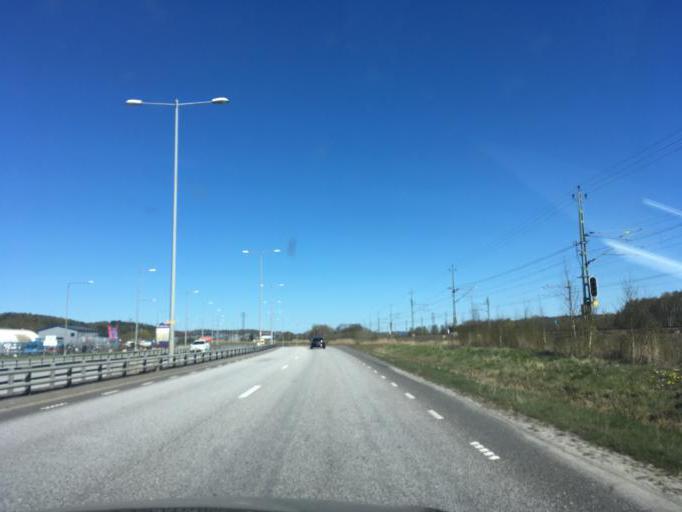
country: SE
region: Vaestra Goetaland
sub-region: Goteborg
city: Eriksbo
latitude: 57.7535
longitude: 12.0053
